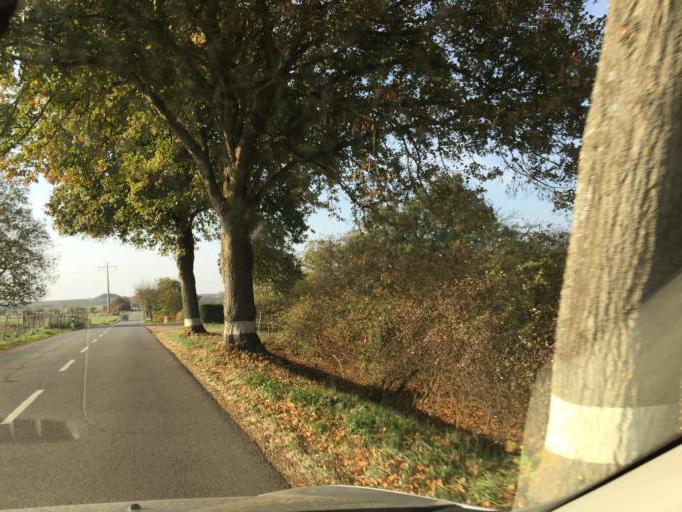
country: LU
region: Grevenmacher
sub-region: Canton de Remich
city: Dalheim
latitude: 49.5300
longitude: 6.2508
